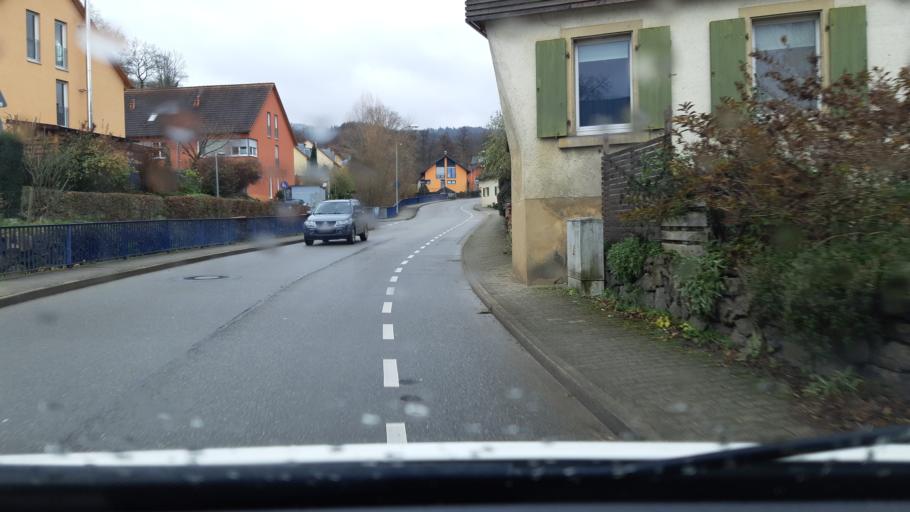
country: DE
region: Baden-Wuerttemberg
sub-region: Freiburg Region
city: Au
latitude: 47.9546
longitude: 7.8285
